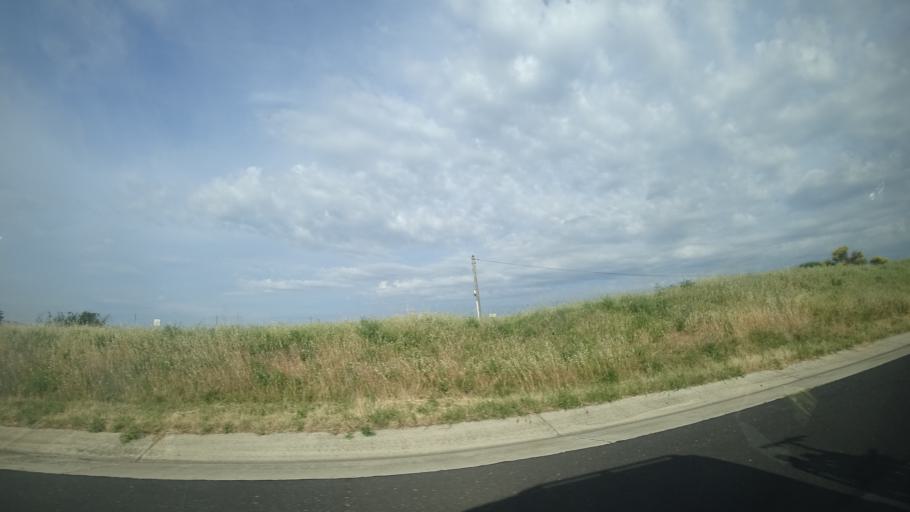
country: FR
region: Languedoc-Roussillon
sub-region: Departement de l'Herault
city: Nebian
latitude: 43.6357
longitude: 3.4473
